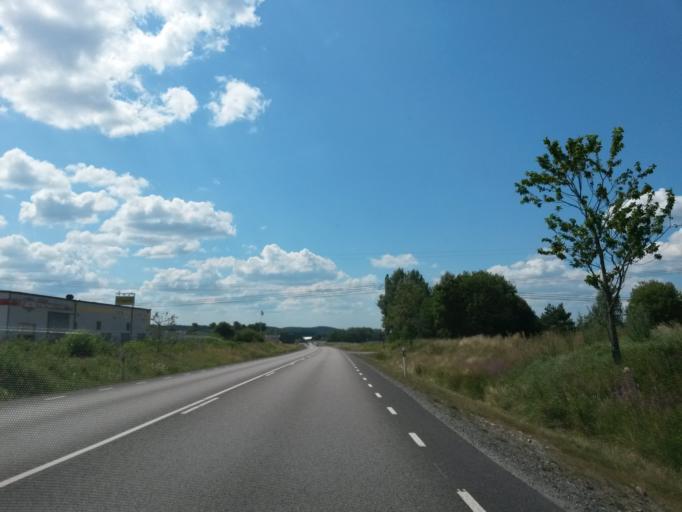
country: SE
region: Vaestra Goetaland
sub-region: Lerums Kommun
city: Grabo
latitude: 57.8412
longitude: 12.2855
